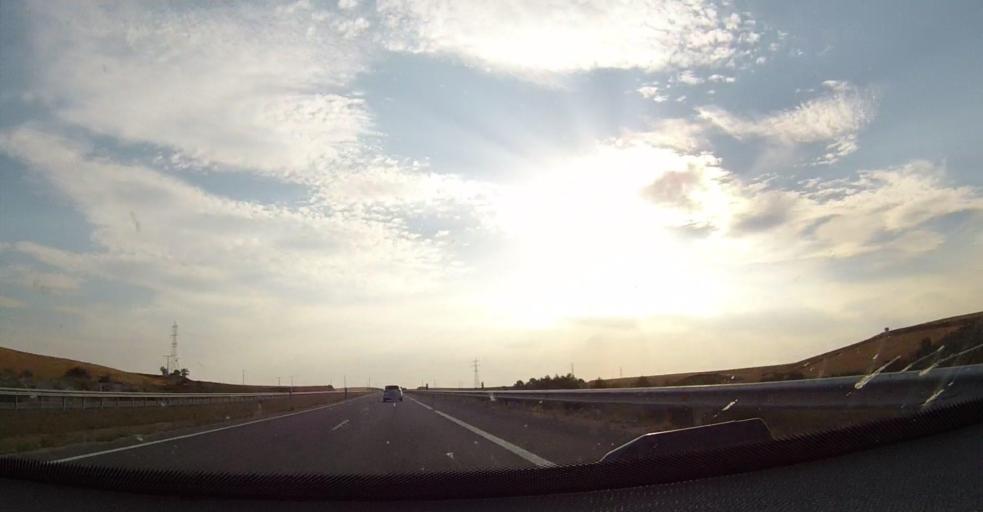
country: ES
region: Castille and Leon
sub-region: Provincia de Burgos
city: Rabe de las Calzadas
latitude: 42.3712
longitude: -3.8654
